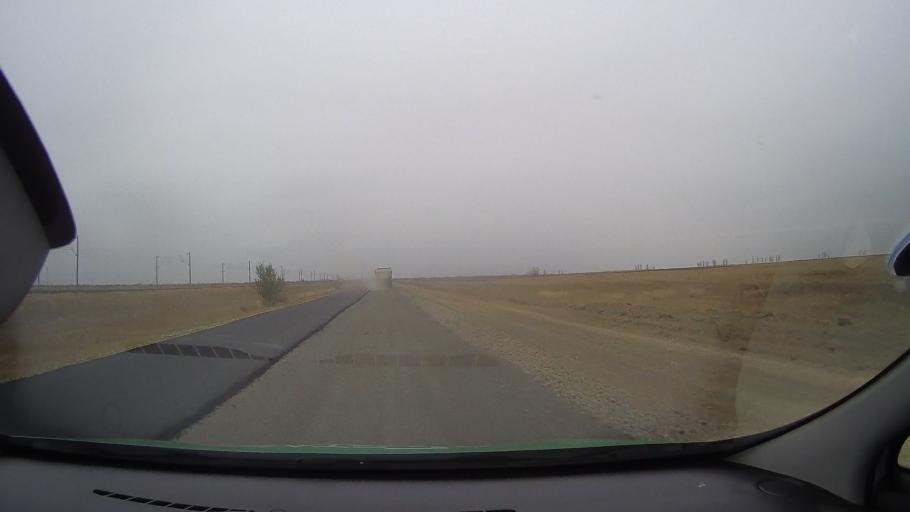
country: RO
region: Braila
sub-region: Comuna Baraganul
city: Baraganul
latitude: 44.7953
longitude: 27.5318
